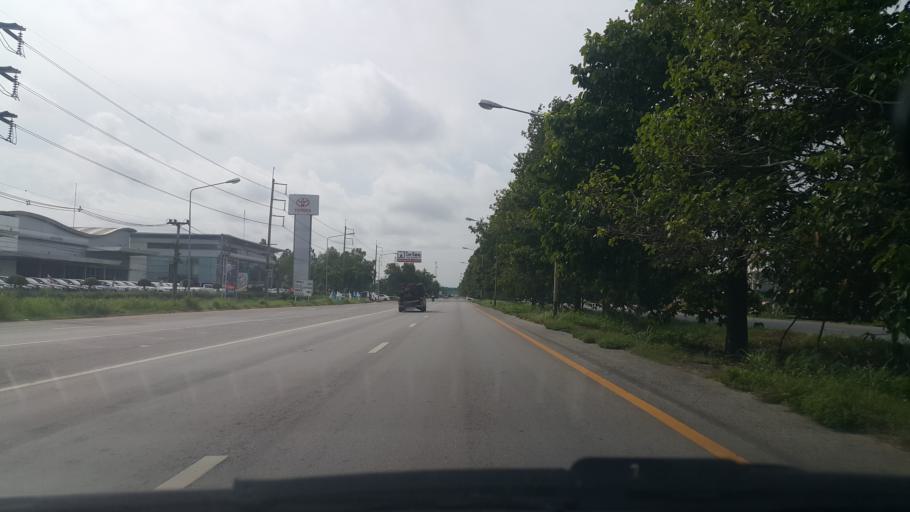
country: TH
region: Rayong
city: Rayong
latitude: 12.6656
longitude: 101.3082
